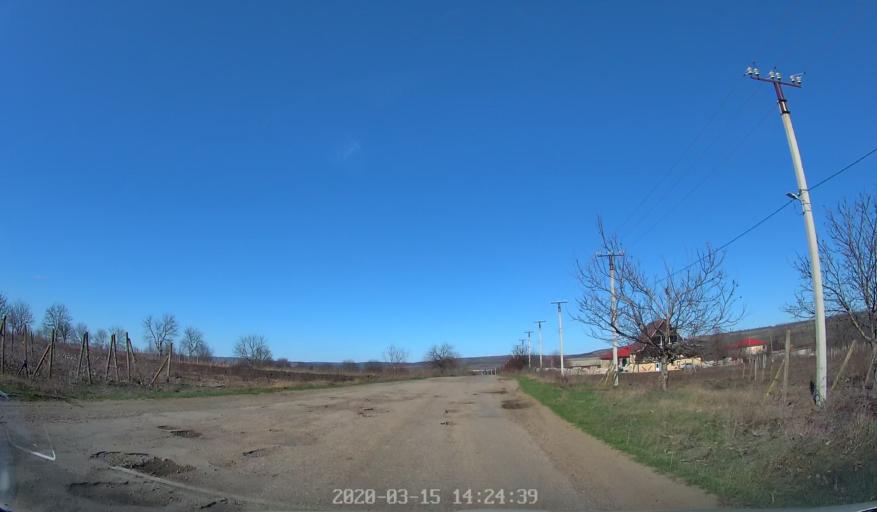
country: MD
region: Orhei
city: Orhei
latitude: 47.3336
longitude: 28.9169
